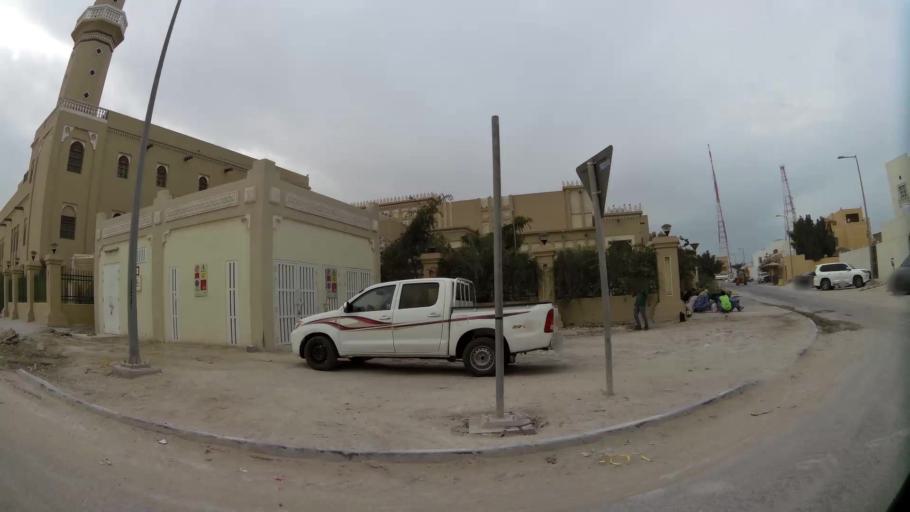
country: QA
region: Baladiyat ad Dawhah
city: Doha
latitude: 25.3076
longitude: 51.5034
